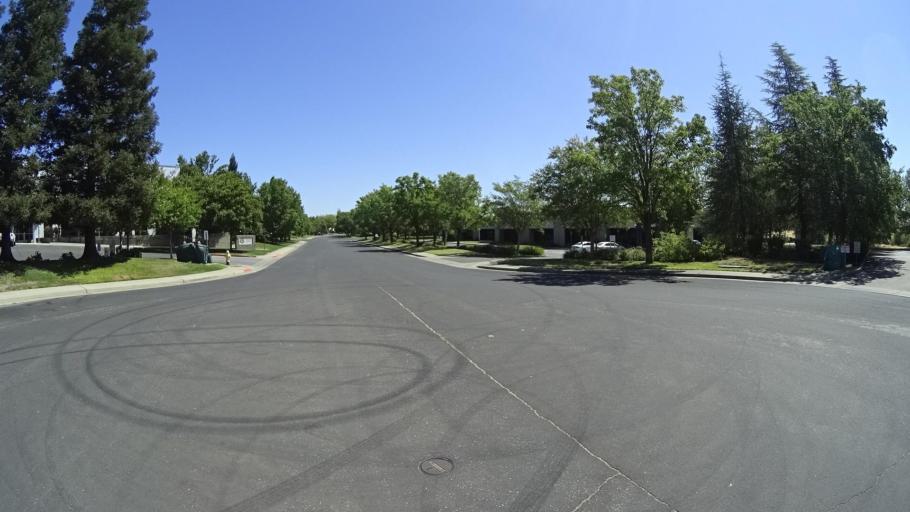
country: US
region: California
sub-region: Placer County
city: Roseville
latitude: 38.8115
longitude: -121.2983
